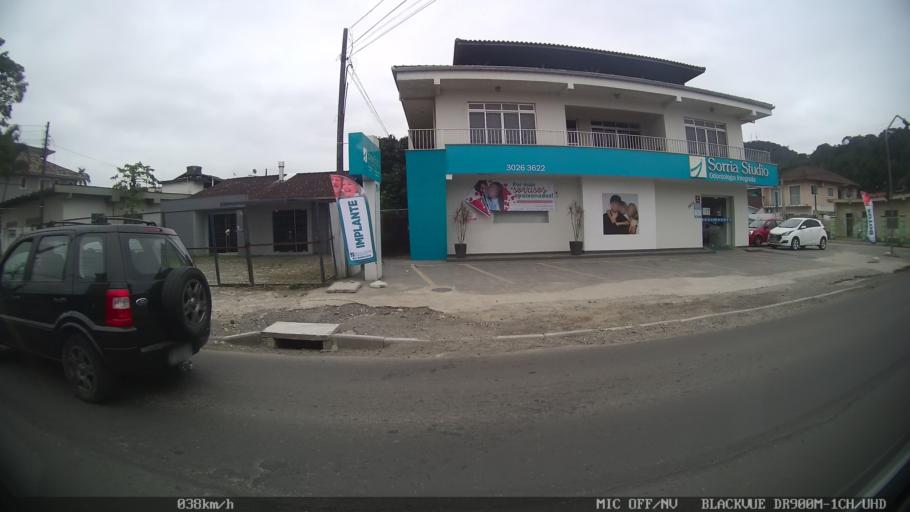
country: BR
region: Santa Catarina
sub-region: Joinville
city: Joinville
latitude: -26.3034
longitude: -48.8268
